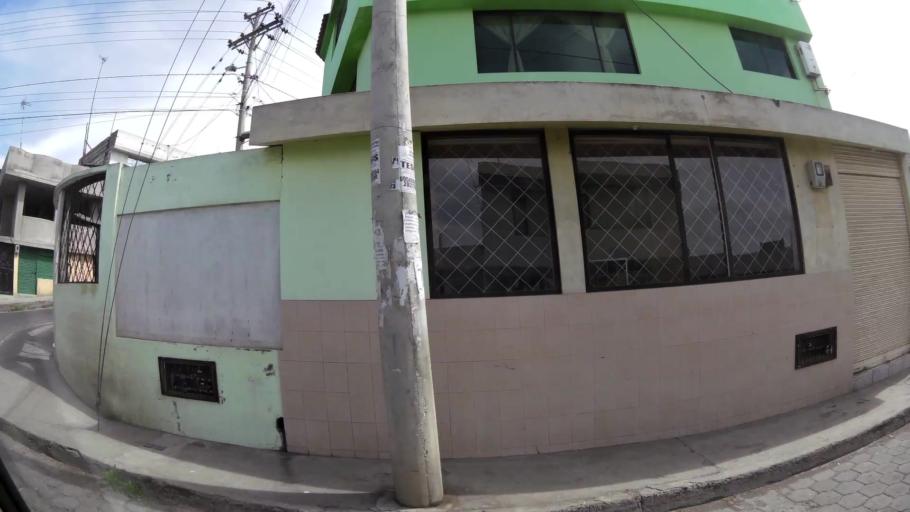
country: EC
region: Cotopaxi
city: Latacunga
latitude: -0.9279
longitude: -78.6075
